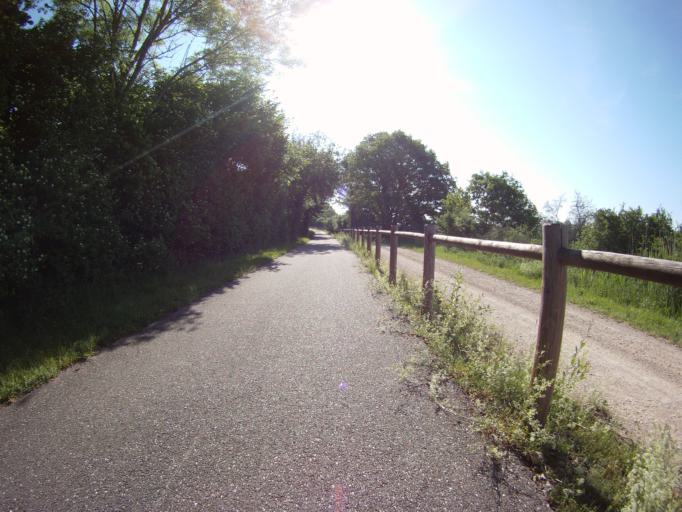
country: FR
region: Lorraine
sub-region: Departement de Meurthe-et-Moselle
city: Champenoux
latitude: 48.7397
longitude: 6.3092
